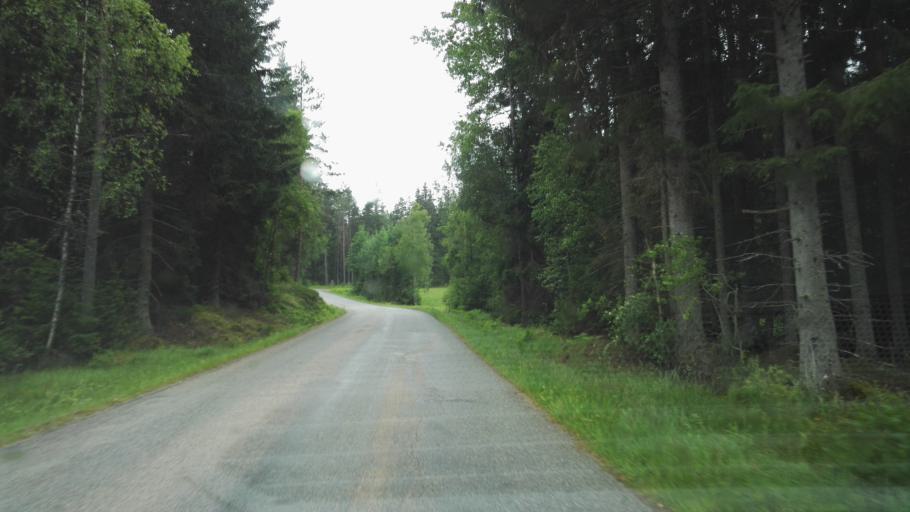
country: SE
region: Joenkoeping
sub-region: Vetlanda Kommun
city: Landsbro
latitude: 57.2777
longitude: 14.8325
